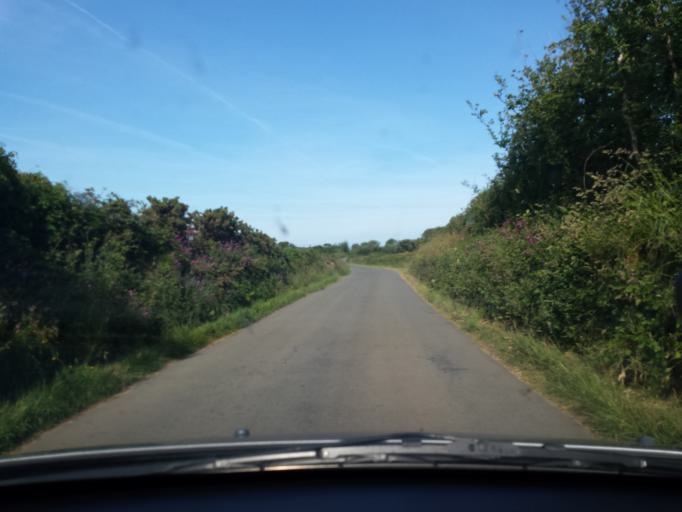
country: FR
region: Lower Normandy
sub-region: Departement de la Manche
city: Beaumont-Hague
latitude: 49.6760
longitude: -1.9199
